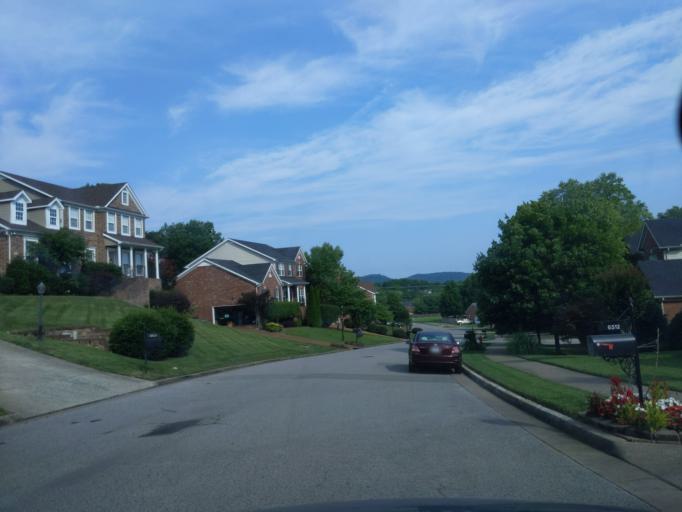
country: US
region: Tennessee
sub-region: Williamson County
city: Brentwood Estates
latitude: 36.0223
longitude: -86.7492
